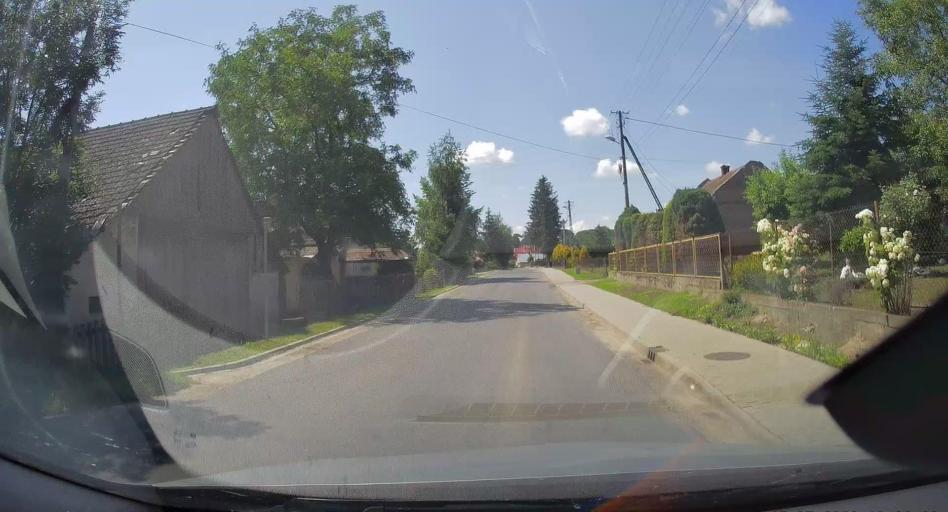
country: PL
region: Subcarpathian Voivodeship
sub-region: Powiat przemyski
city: Medyka
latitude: 49.8431
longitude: 22.8859
